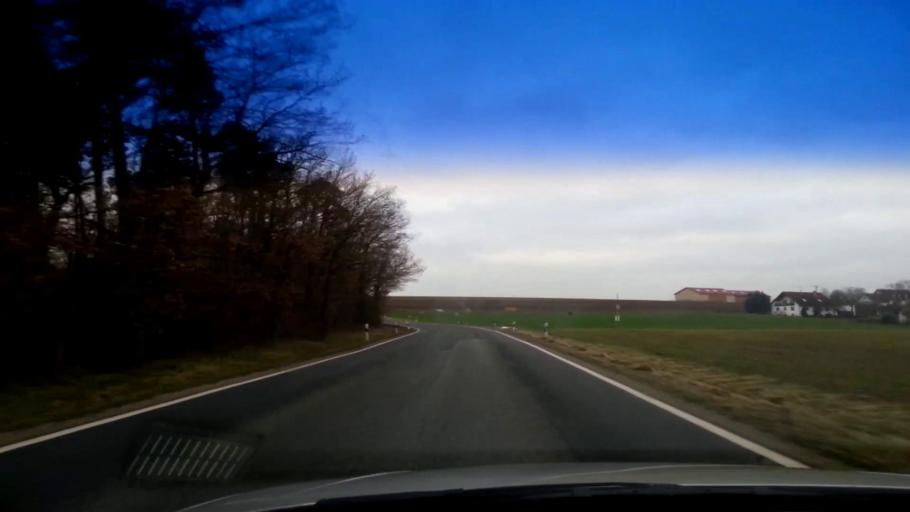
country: DE
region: Bavaria
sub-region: Upper Franconia
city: Burgebrach
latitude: 49.8070
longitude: 10.7830
